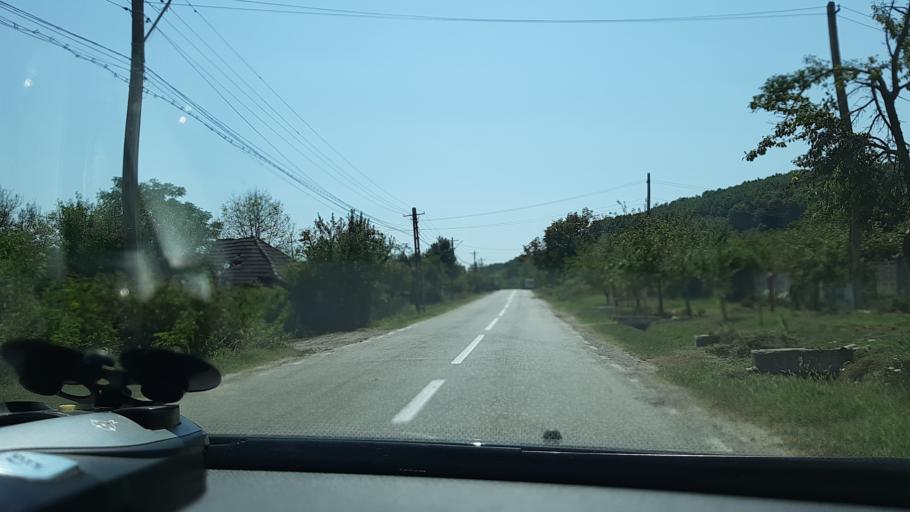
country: RO
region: Gorj
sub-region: Comuna Hurezani
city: Hurezani
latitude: 44.8291
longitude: 23.6432
